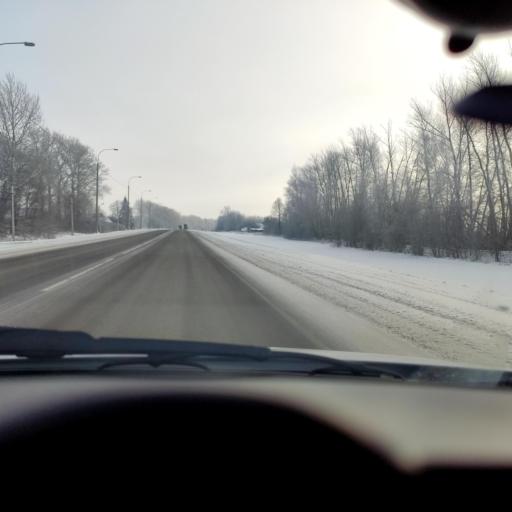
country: RU
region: Kursk
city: Kirovskiy
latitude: 51.6765
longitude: 36.5972
